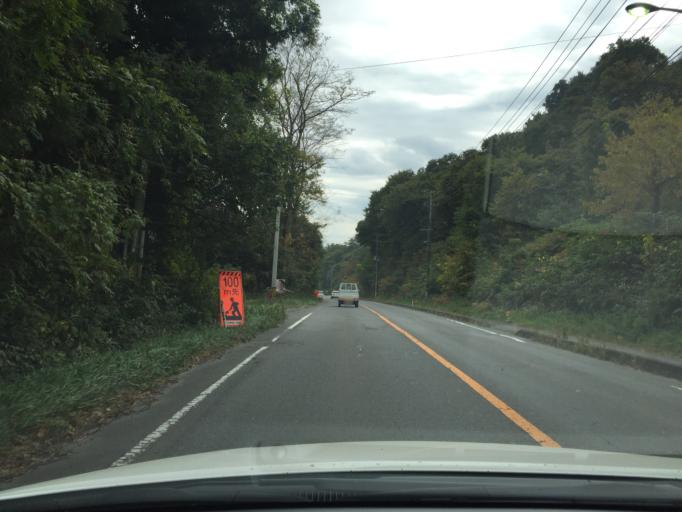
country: JP
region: Fukushima
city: Ishikawa
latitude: 37.0495
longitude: 140.3739
